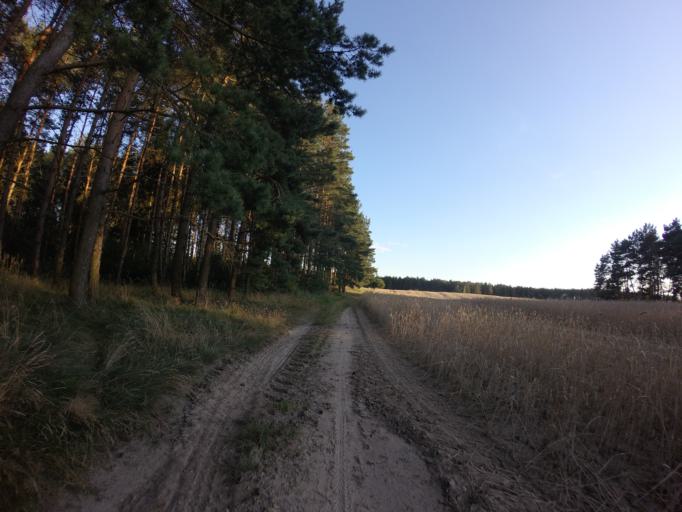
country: PL
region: West Pomeranian Voivodeship
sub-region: Powiat choszczenski
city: Choszczno
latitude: 53.2074
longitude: 15.4230
